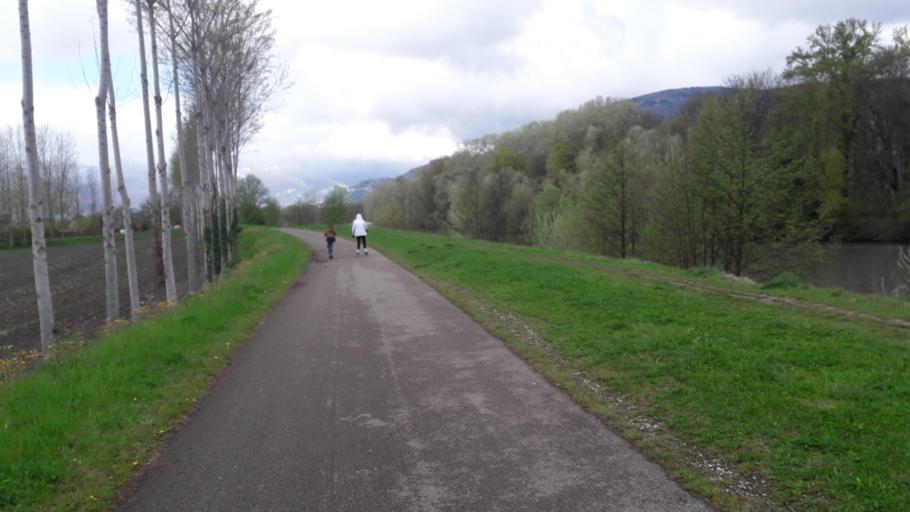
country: FR
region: Rhone-Alpes
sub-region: Departement de l'Isere
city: Gieres
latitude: 45.1889
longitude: 5.7950
